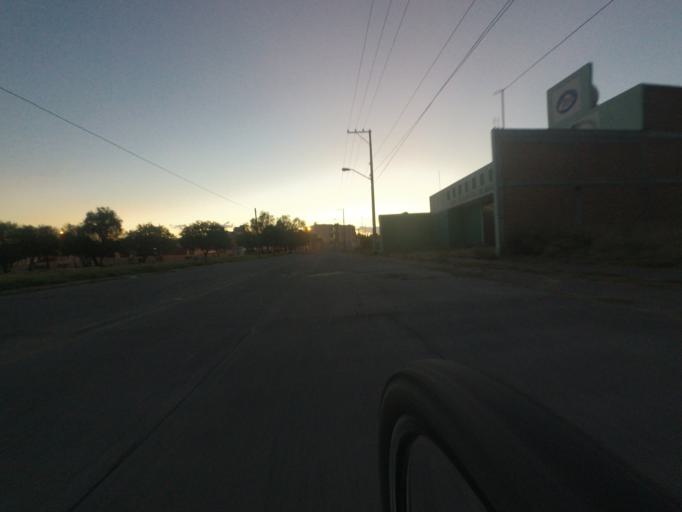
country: MX
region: Aguascalientes
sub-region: Aguascalientes
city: La Loma de los Negritos
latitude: 21.8536
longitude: -102.3345
